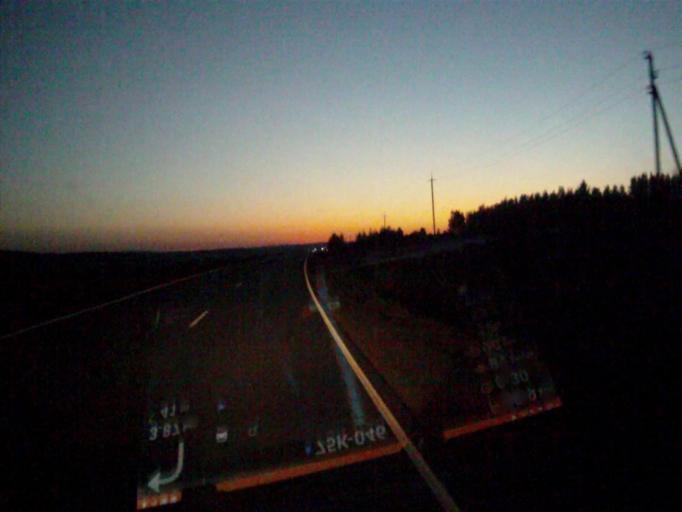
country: RU
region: Chelyabinsk
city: Chebarkul'
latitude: 55.2203
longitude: 60.5095
